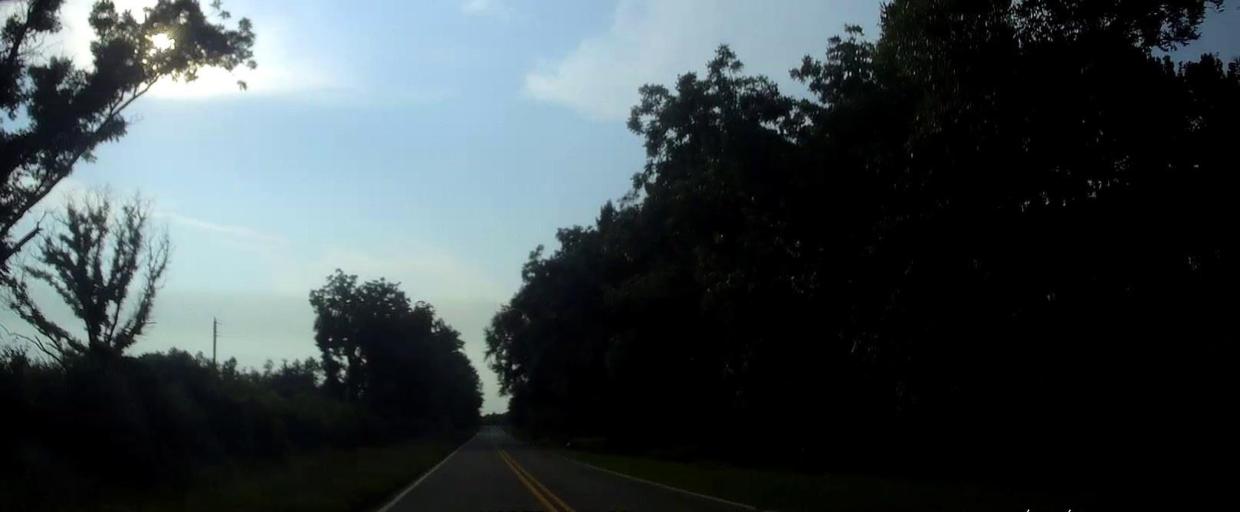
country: US
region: Georgia
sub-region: Laurens County
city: Dublin
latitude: 32.4840
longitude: -82.9711
